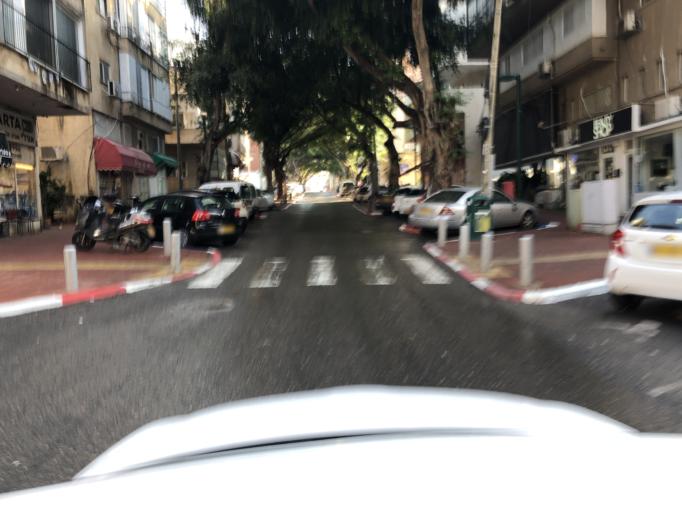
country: IL
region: Tel Aviv
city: Ramat Gan
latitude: 32.0913
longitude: 34.8185
